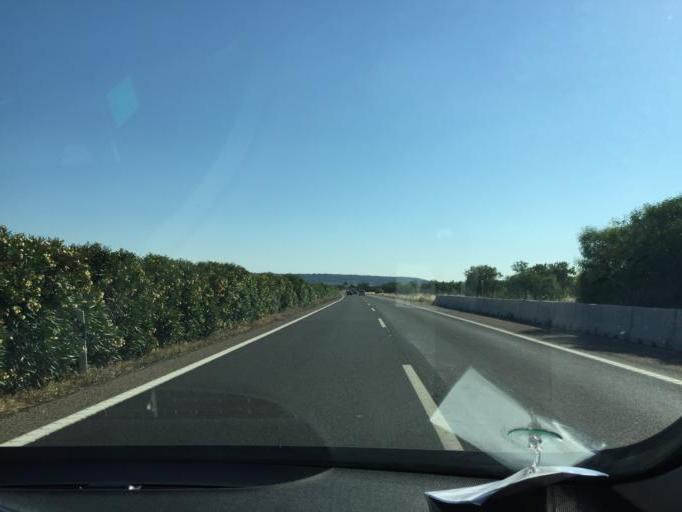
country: ES
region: Balearic Islands
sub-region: Illes Balears
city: Consell
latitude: 39.6606
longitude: 2.8089
